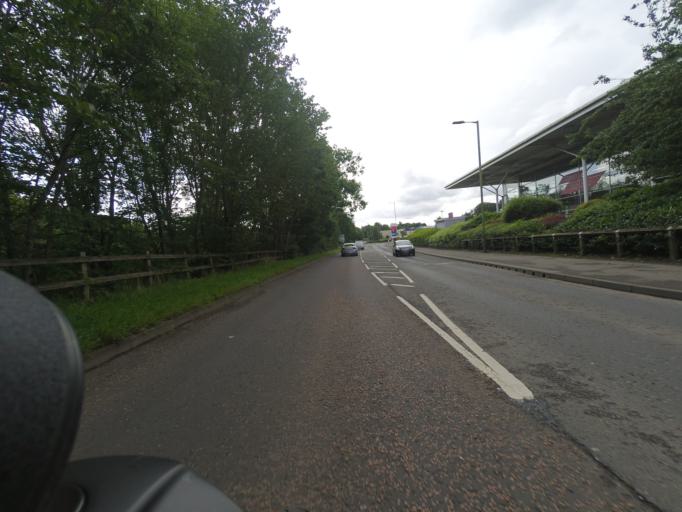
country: GB
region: Scotland
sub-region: Perth and Kinross
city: Blairgowrie
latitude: 56.5900
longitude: -3.3344
